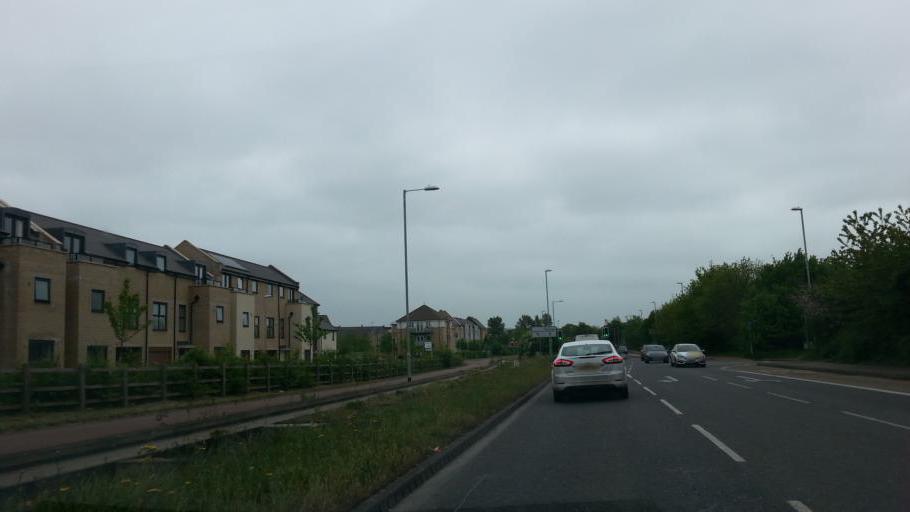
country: GB
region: England
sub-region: Cambridgeshire
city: Histon
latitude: 52.2325
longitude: 0.1133
